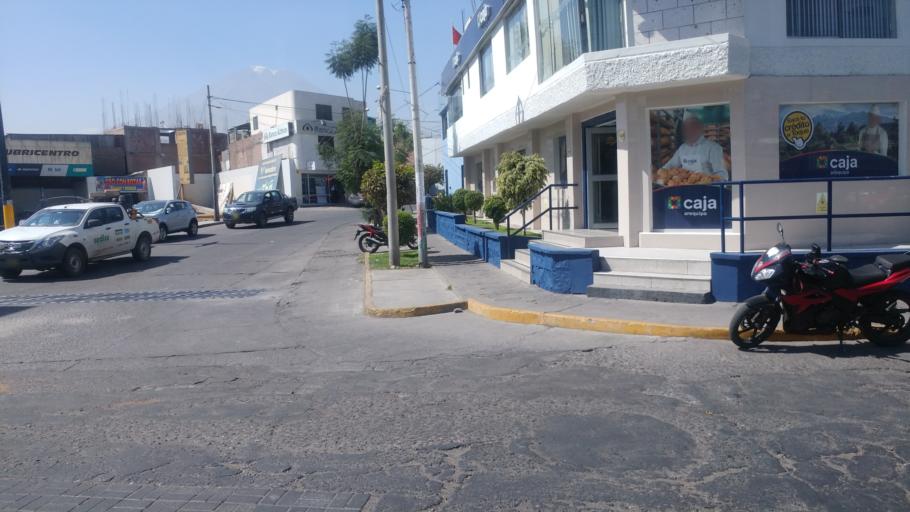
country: PE
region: Arequipa
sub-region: Provincia de Arequipa
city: Arequipa
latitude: -16.4120
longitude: -71.5126
